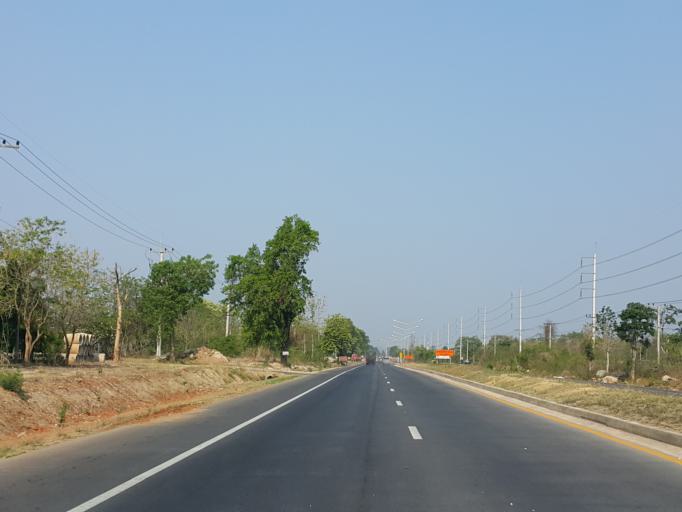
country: TH
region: Kanchanaburi
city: Kanchanaburi
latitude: 14.0872
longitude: 99.3604
